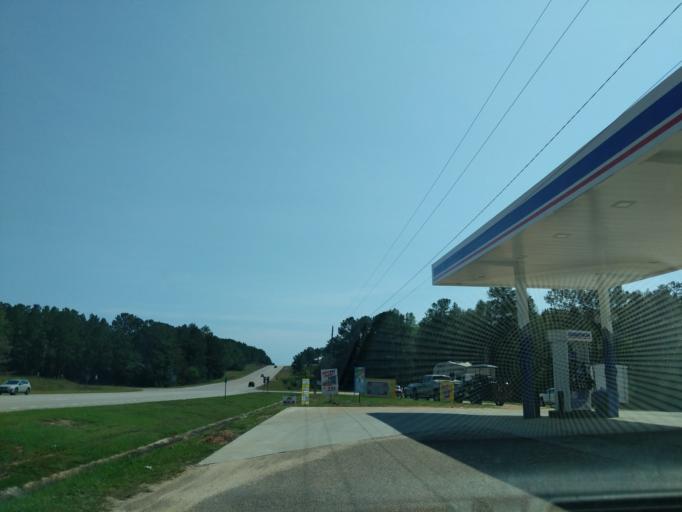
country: US
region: Alabama
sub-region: Butler County
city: Georgiana
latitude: 31.4884
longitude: -86.6834
